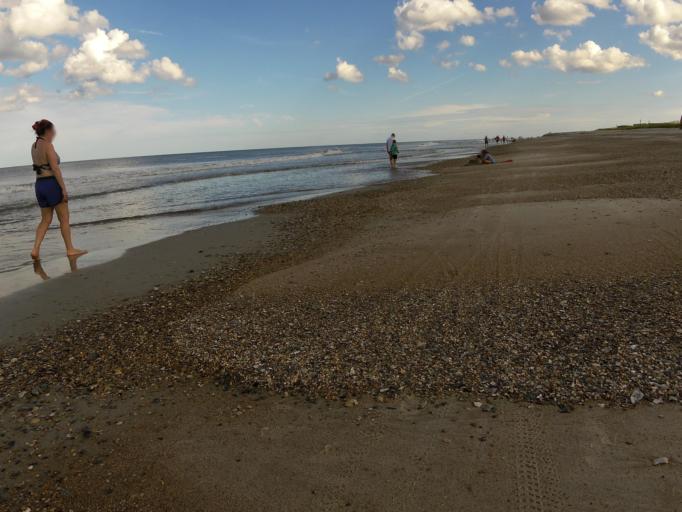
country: US
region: Florida
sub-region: Nassau County
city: Fernandina Beach
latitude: 30.6851
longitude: -81.4280
